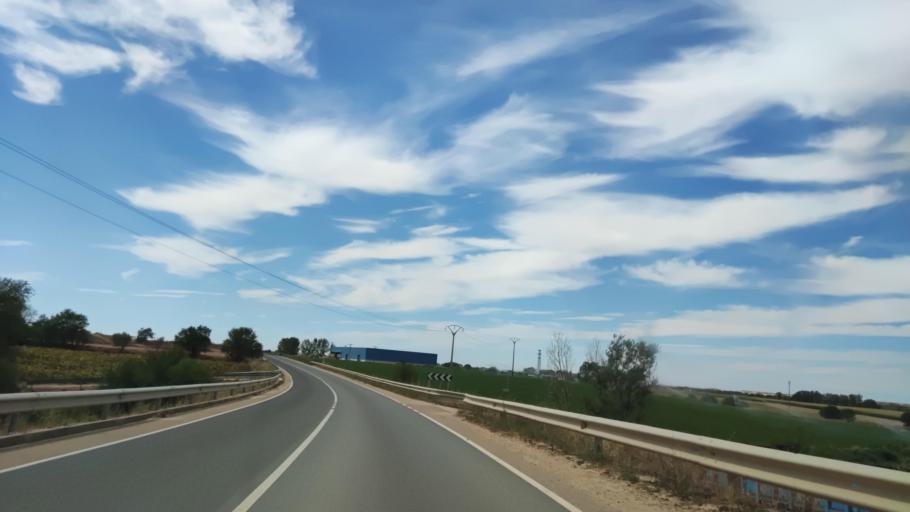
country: ES
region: Castille and Leon
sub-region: Provincia de Zamora
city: Madridanos
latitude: 41.4912
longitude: -5.6249
